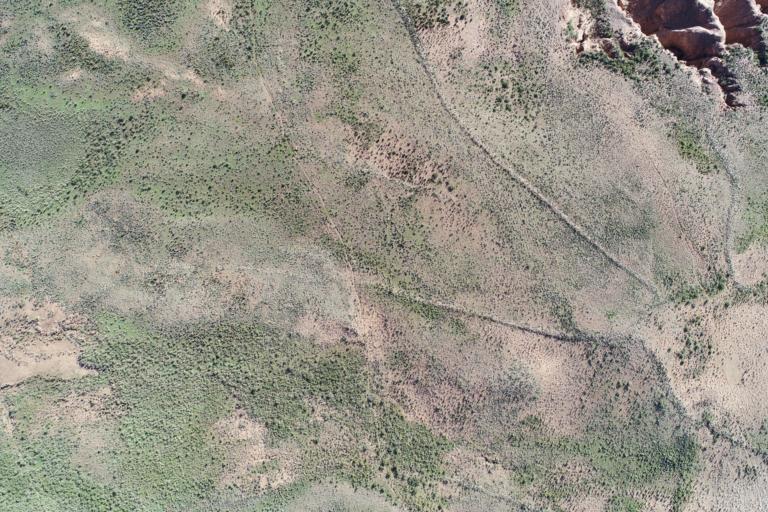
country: BO
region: La Paz
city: Curahuara de Carangas
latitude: -17.3043
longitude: -68.5016
